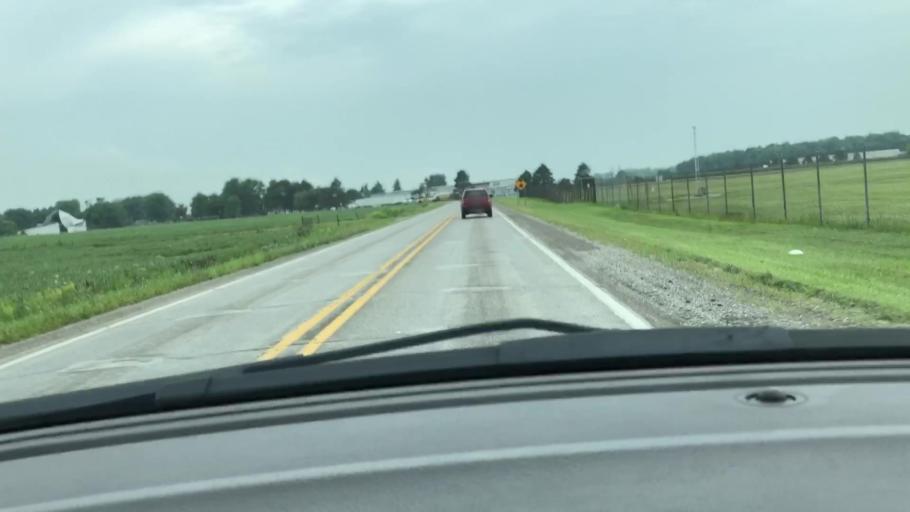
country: US
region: Michigan
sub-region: Saginaw County
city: Freeland
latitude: 43.5232
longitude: -84.0932
